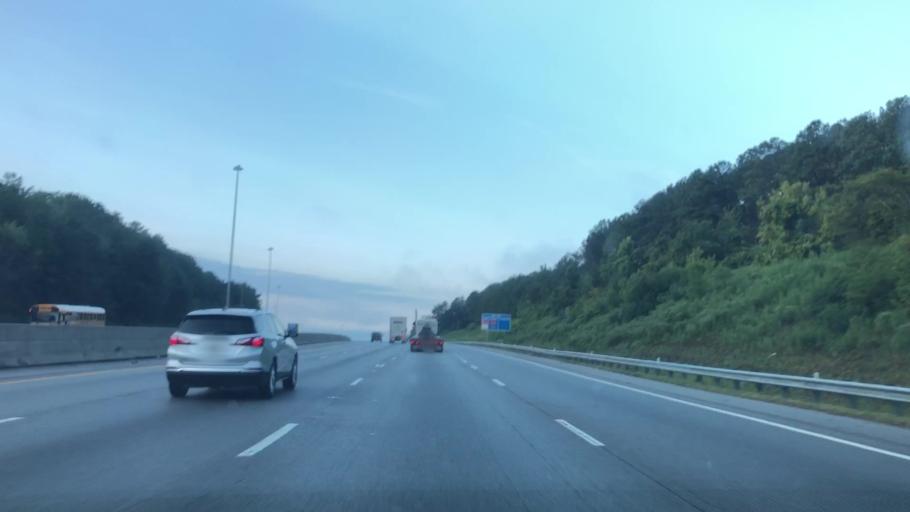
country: US
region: Alabama
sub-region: Shelby County
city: Indian Springs Village
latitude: 33.3512
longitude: -86.7803
